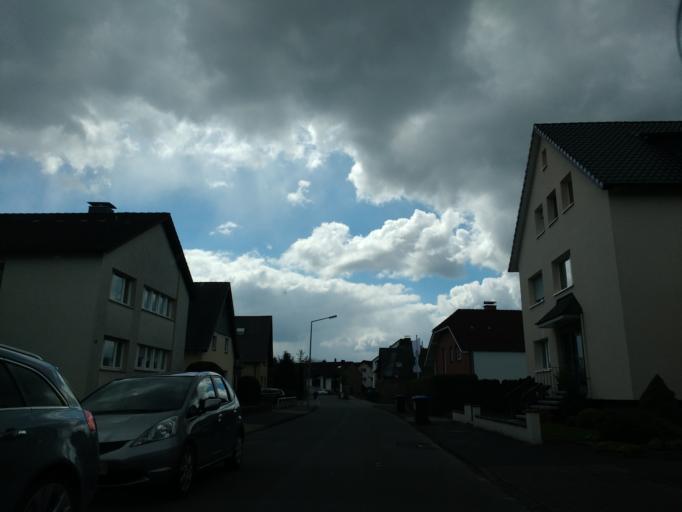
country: DE
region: North Rhine-Westphalia
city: Bad Lippspringe
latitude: 51.7901
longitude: 8.8244
